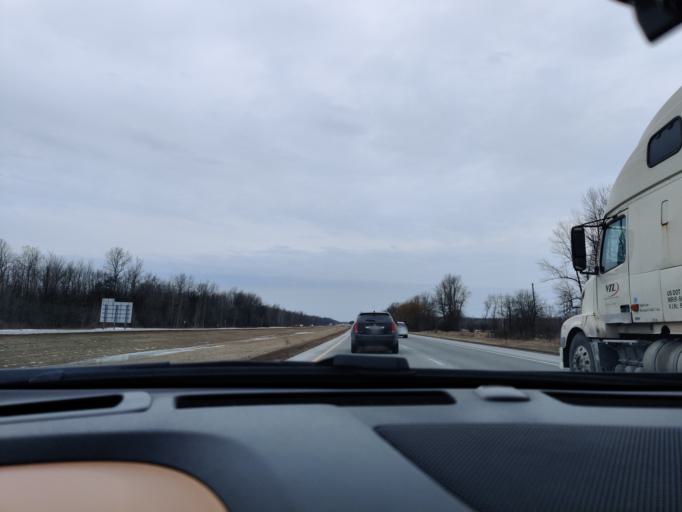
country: US
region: New York
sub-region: St. Lawrence County
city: Norfolk
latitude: 44.9354
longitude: -75.1552
